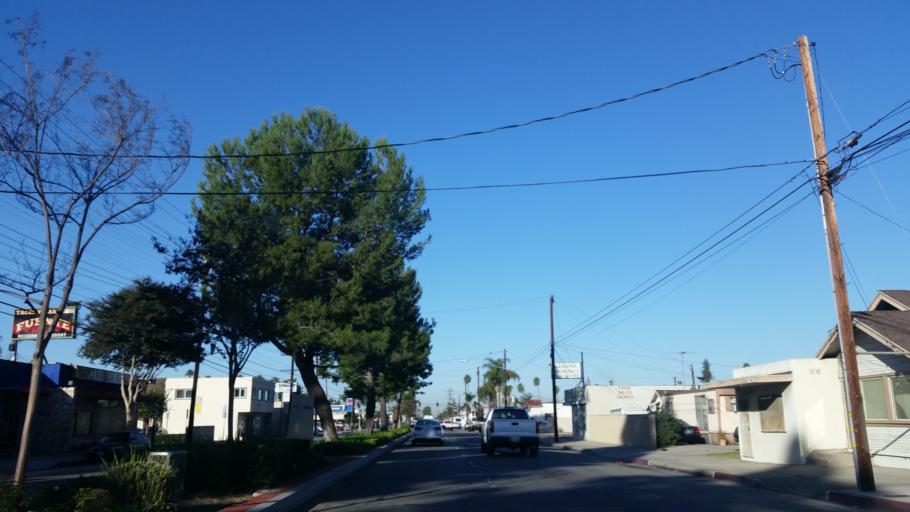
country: US
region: California
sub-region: Los Angeles County
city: Bellflower
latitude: 33.8748
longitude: -118.1315
